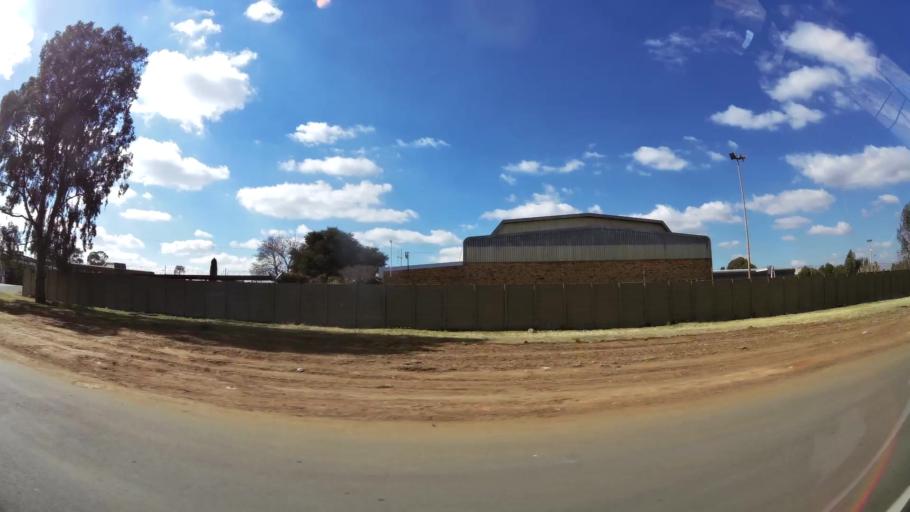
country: ZA
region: Gauteng
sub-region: West Rand District Municipality
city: Krugersdorp
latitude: -26.1287
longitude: 27.8021
